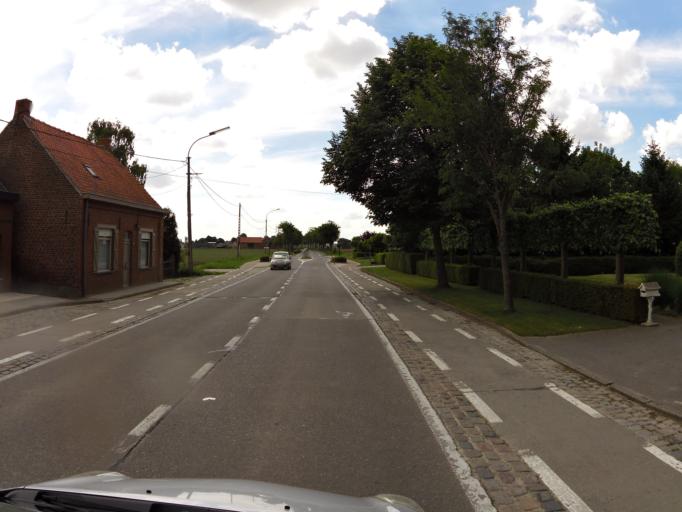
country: BE
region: Flanders
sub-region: Provincie West-Vlaanderen
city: Zonnebeke
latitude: 50.8865
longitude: 2.9326
